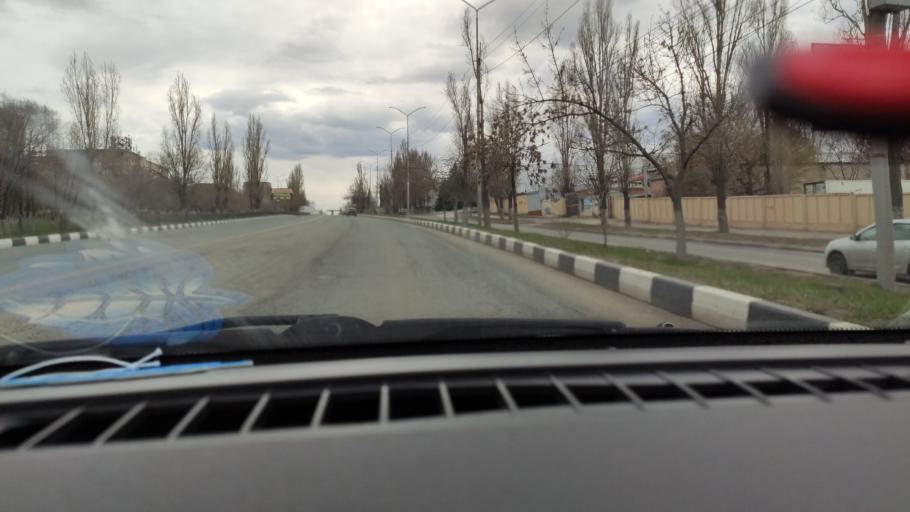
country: RU
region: Saratov
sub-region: Saratovskiy Rayon
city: Saratov
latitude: 51.6083
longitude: 45.9693
